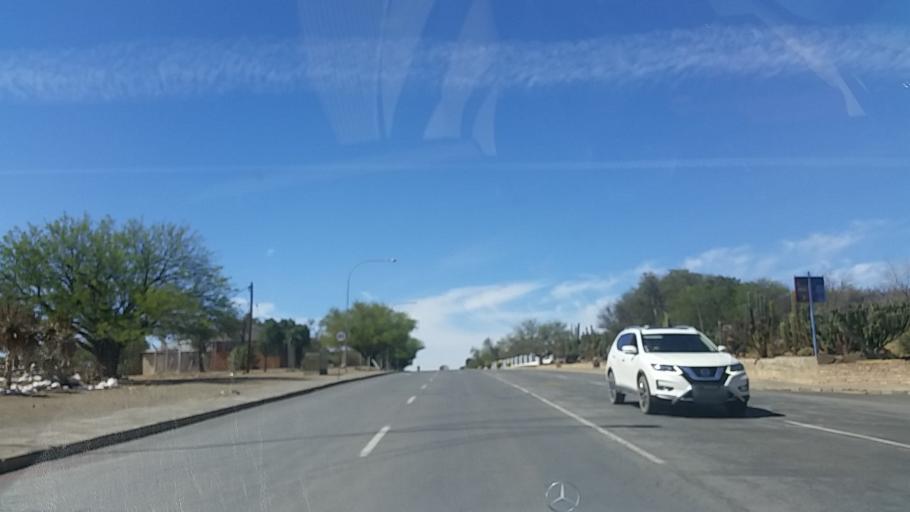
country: ZA
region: Eastern Cape
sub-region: Cacadu District Municipality
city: Graaff-Reinet
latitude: -32.2591
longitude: 24.5387
